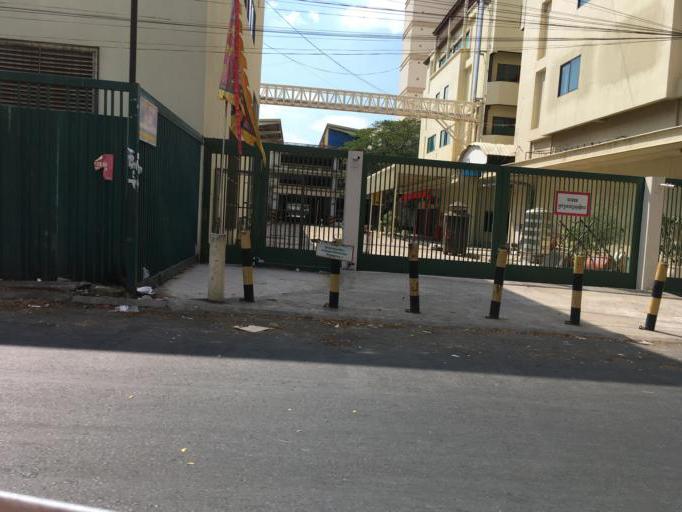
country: KH
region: Phnom Penh
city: Phnom Penh
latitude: 11.5495
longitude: 104.9034
